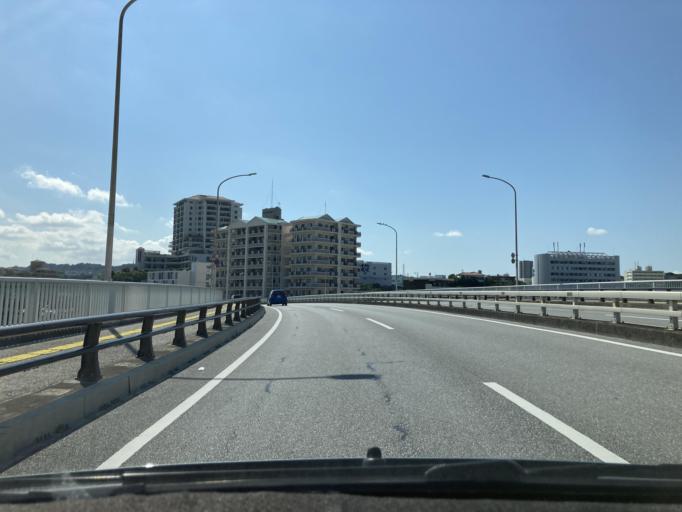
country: JP
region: Okinawa
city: Ginowan
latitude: 26.2709
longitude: 127.7260
